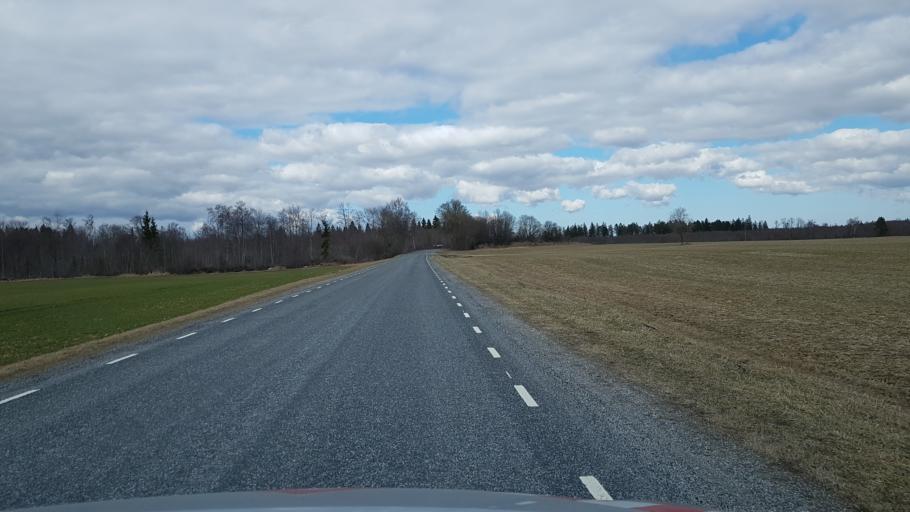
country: EE
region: Laeaene-Virumaa
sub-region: Tamsalu vald
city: Tamsalu
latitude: 59.1814
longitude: 26.1276
